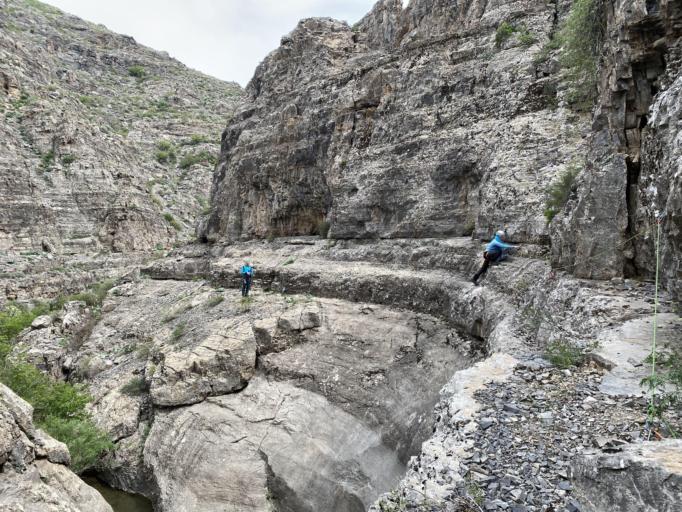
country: KZ
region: Ongtustik Qazaqstan
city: Ashchysay
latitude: 43.5326
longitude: 68.8439
